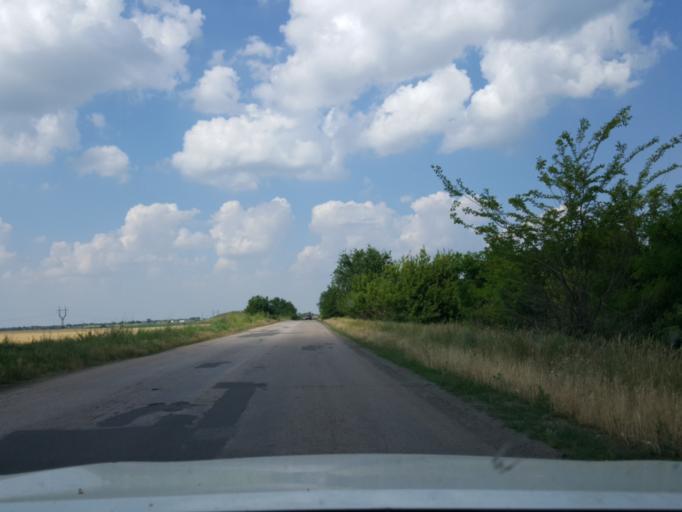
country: UA
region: Odessa
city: Starokozache
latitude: 46.3873
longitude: 30.0887
